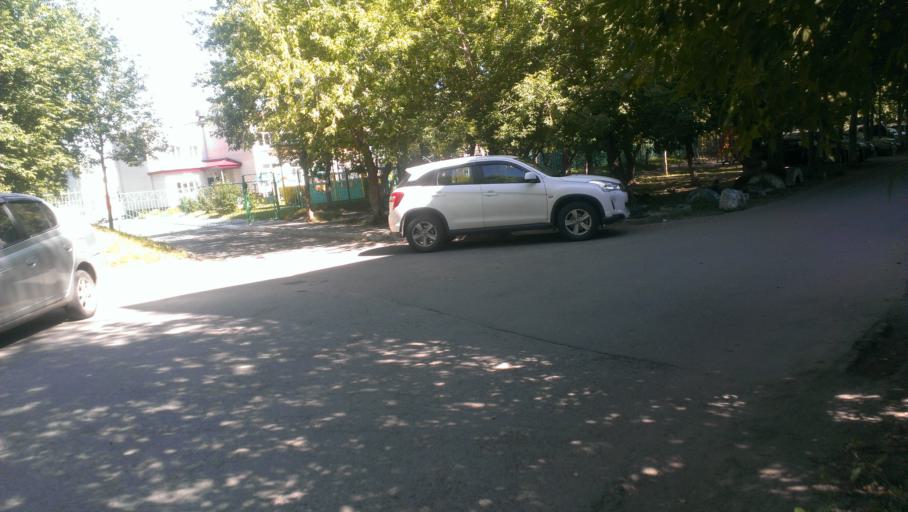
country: RU
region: Altai Krai
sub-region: Gorod Barnaulskiy
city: Barnaul
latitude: 53.3611
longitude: 83.6956
